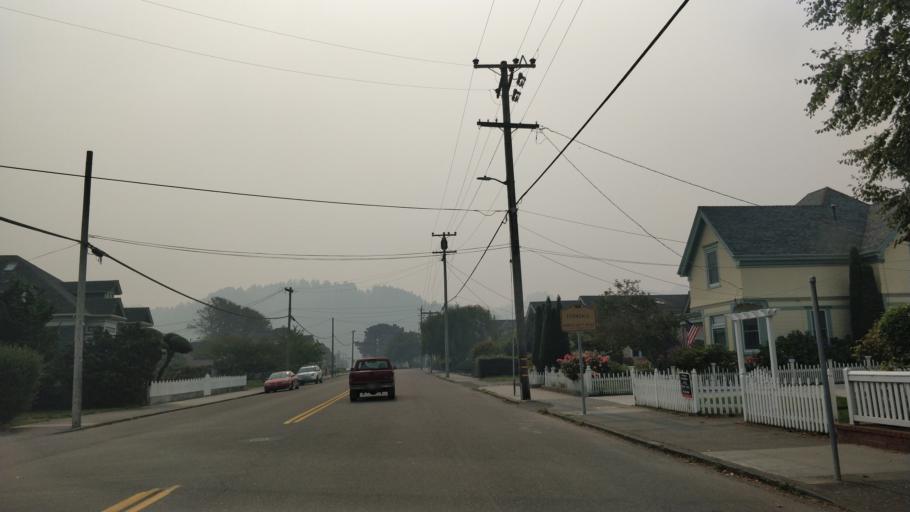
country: US
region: California
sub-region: Humboldt County
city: Ferndale
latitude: 40.5827
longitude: -124.2598
